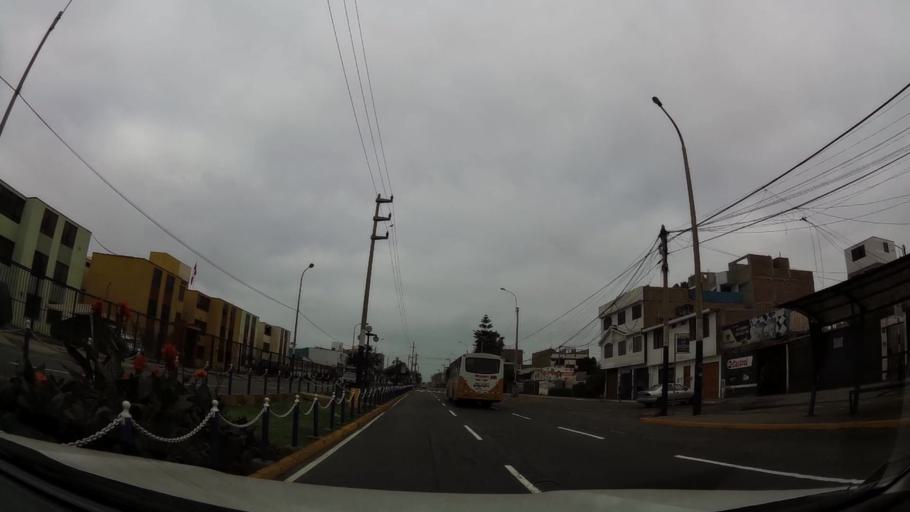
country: PE
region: Lima
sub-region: Lima
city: Surco
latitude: -12.2037
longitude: -77.0160
